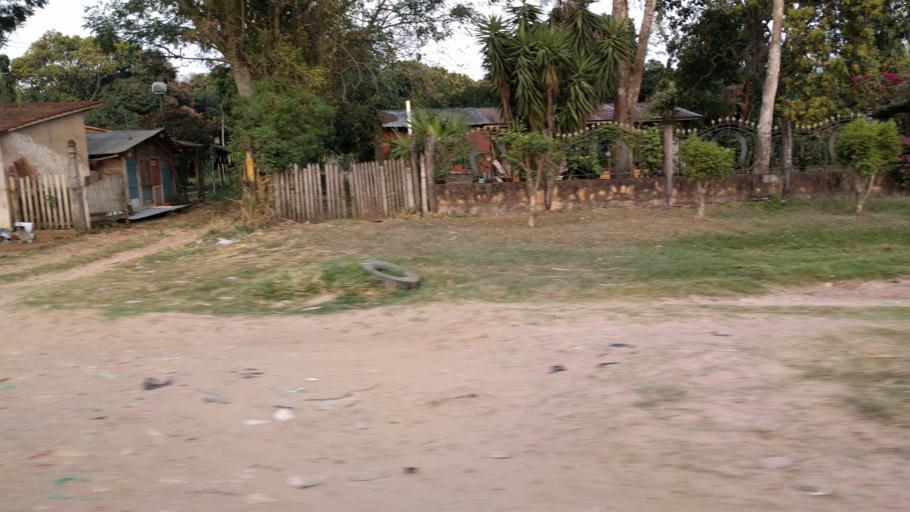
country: BO
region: Santa Cruz
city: Santa Rita
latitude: -17.9544
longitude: -63.3570
